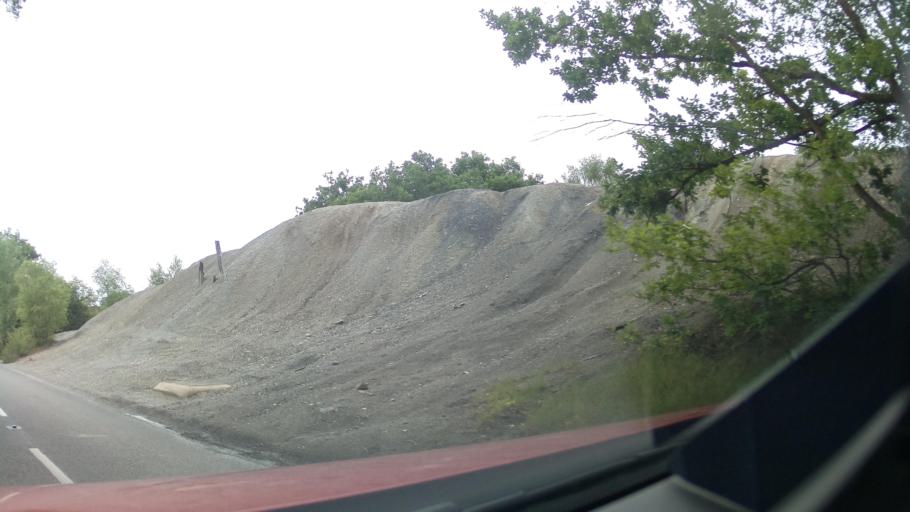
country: GB
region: England
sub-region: Devon
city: Chudleigh
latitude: 50.6348
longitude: -3.6395
